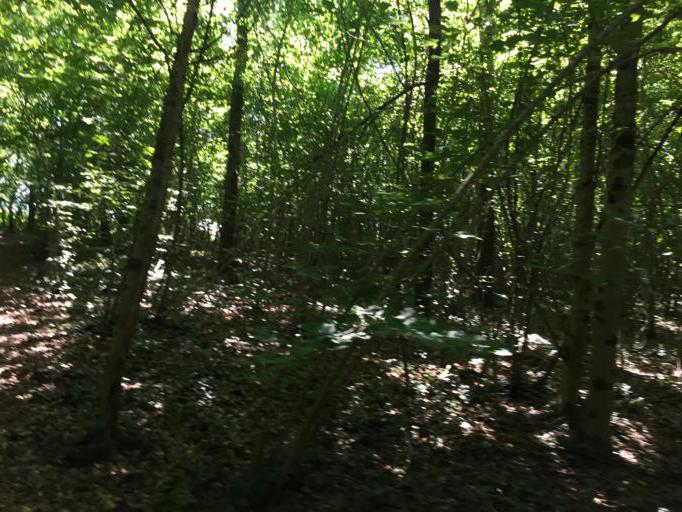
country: FR
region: Bourgogne
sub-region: Departement de l'Yonne
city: Fontenailles
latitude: 47.5904
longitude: 3.3396
